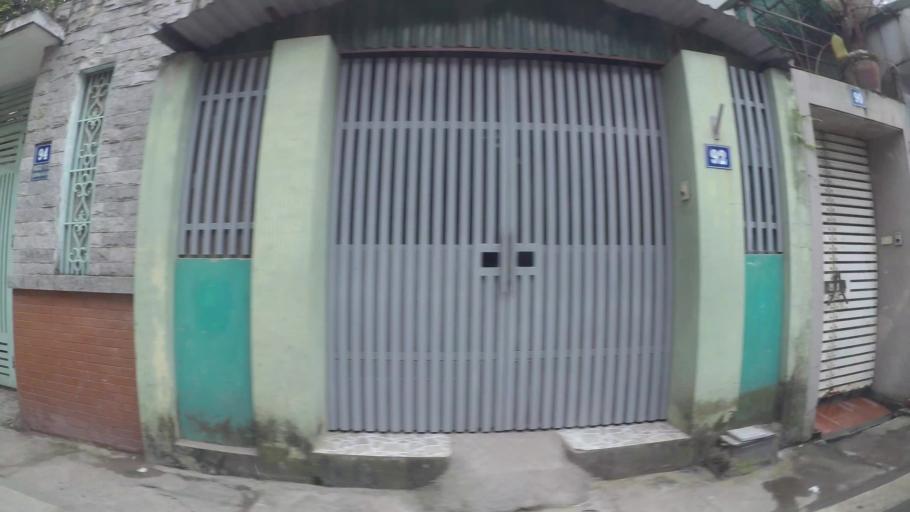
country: VN
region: Ha Noi
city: Tay Ho
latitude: 21.0671
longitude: 105.8328
